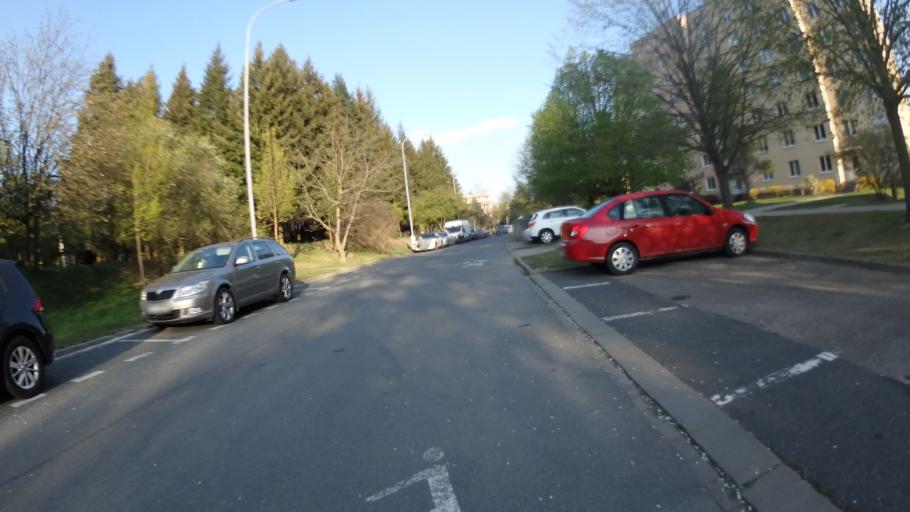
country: CZ
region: South Moravian
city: Moravany
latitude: 49.1731
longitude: 16.5758
